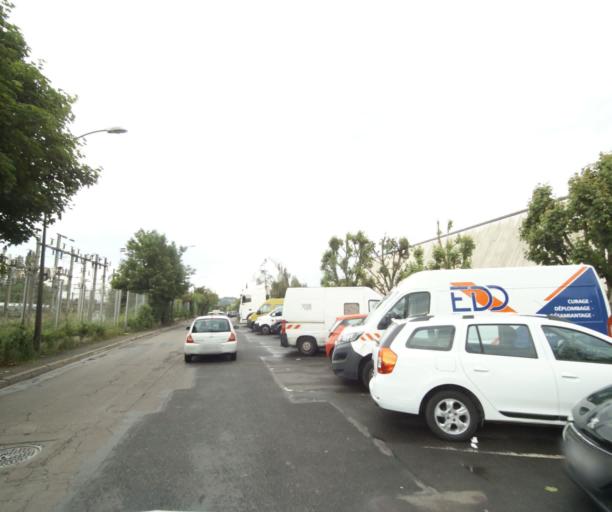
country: FR
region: Ile-de-France
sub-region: Departement du Val-d'Oise
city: Argenteuil
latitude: 48.9501
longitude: 2.2322
